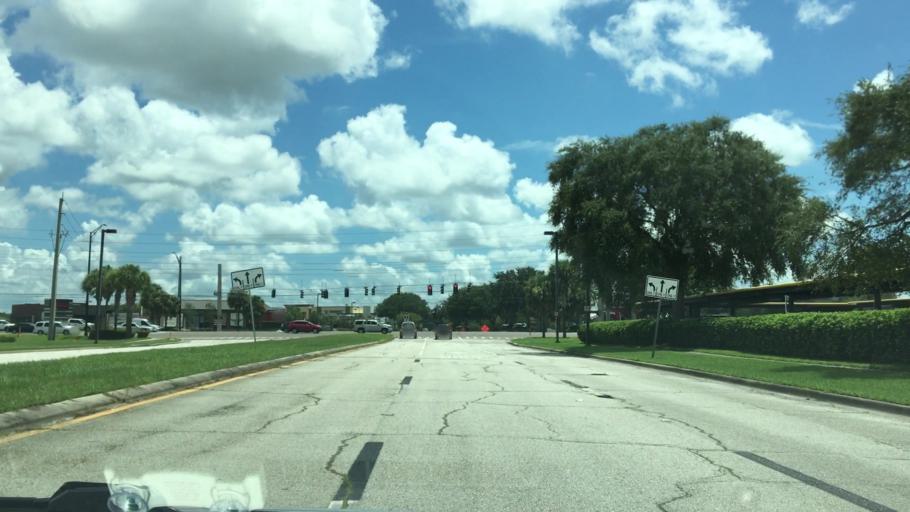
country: US
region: Florida
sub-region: Orange County
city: Conway
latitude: 28.4631
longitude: -81.3113
